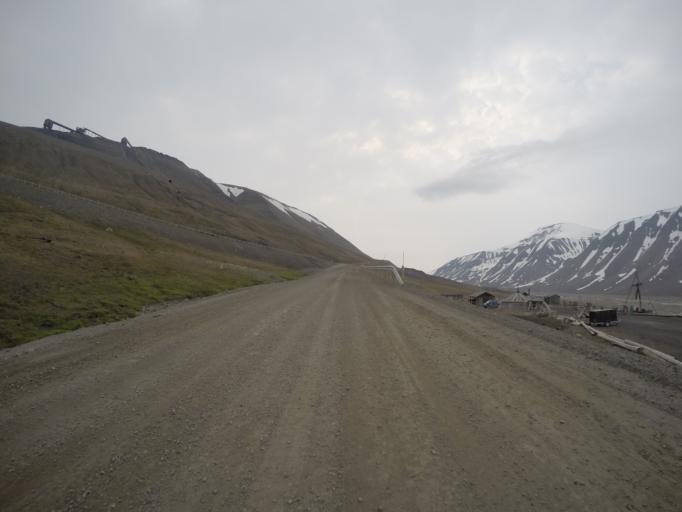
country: SJ
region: Svalbard
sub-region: Spitsbergen
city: Longyearbyen
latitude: 78.1604
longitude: 16.0024
